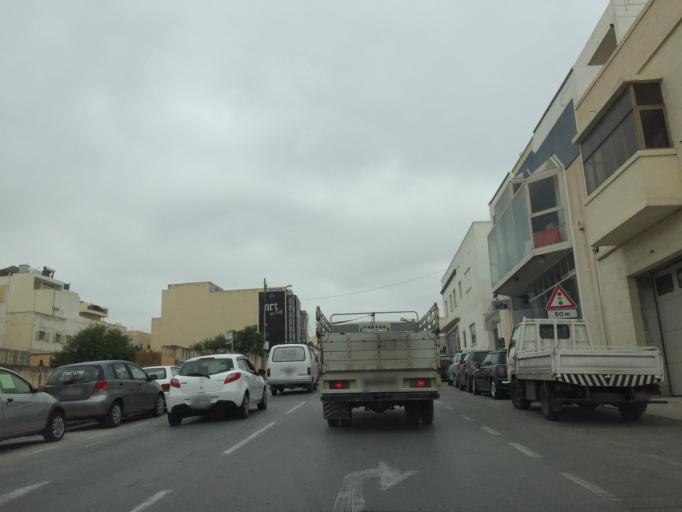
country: MT
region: Attard
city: Attard
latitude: 35.8893
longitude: 14.4404
